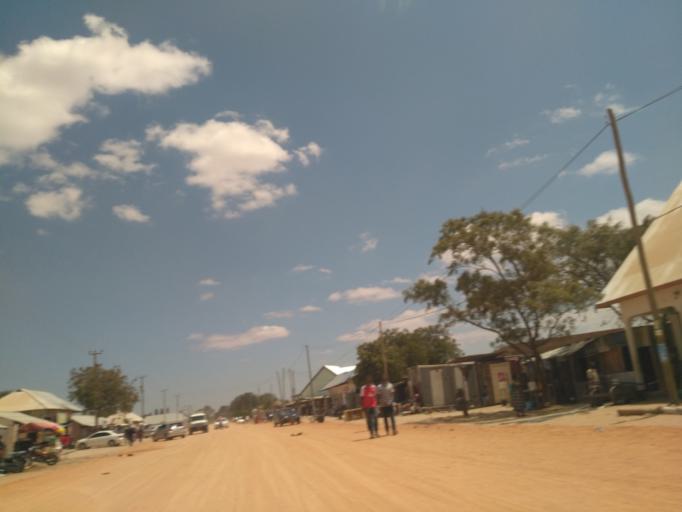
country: TZ
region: Dodoma
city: Kisasa
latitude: -6.1657
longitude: 35.7839
